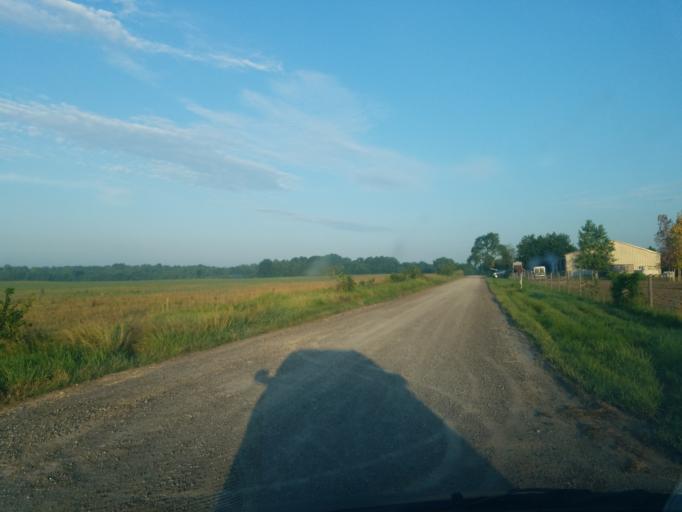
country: US
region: Indiana
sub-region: Allen County
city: Harlan
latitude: 41.2697
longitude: -84.8668
